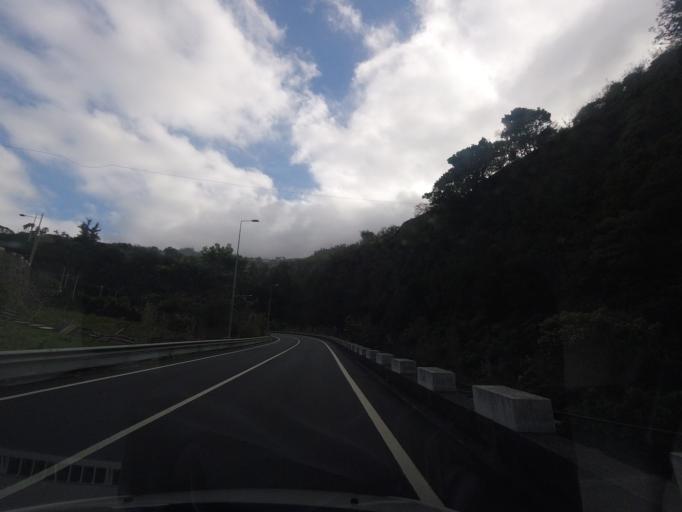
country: PT
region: Madeira
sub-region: Sao Vicente
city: Sao Vicente
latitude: 32.7969
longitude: -17.0411
